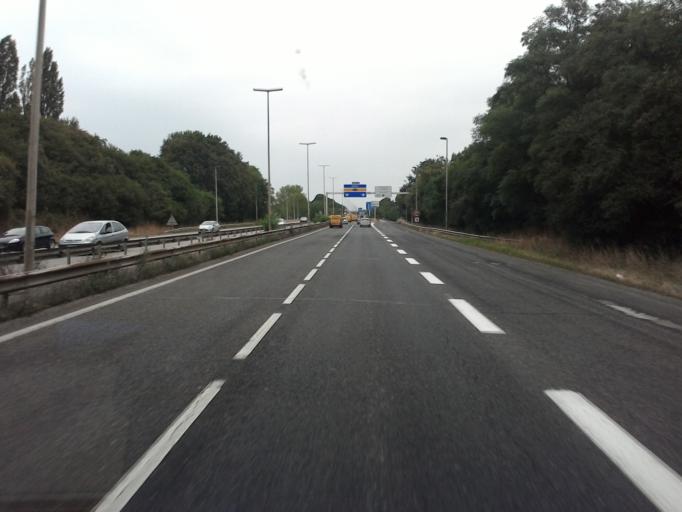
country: FR
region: Lorraine
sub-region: Departement de Meurthe-et-Moselle
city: Richardmenil
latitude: 48.6143
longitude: 6.1784
